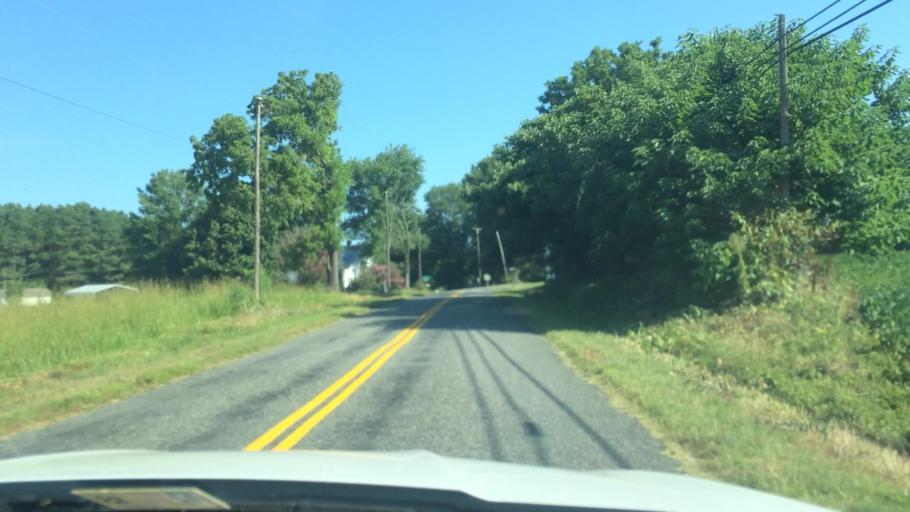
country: US
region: Virginia
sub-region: Richmond County
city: Warsaw
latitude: 37.8847
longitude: -76.6251
